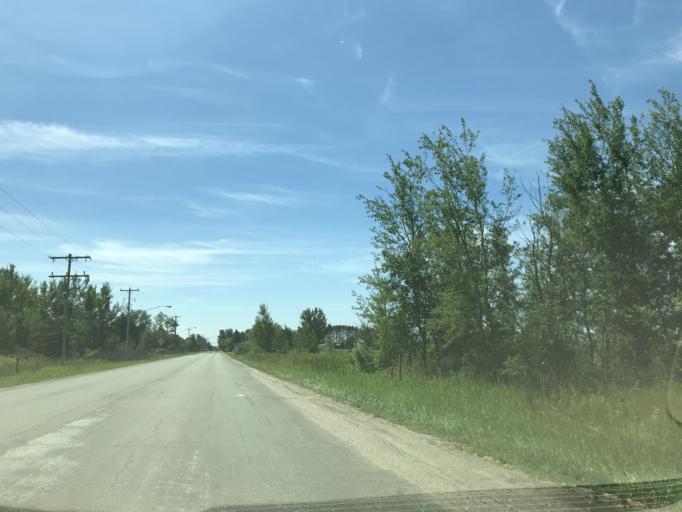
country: US
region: Michigan
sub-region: Roscommon County
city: Houghton Lake
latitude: 44.3357
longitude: -84.9447
